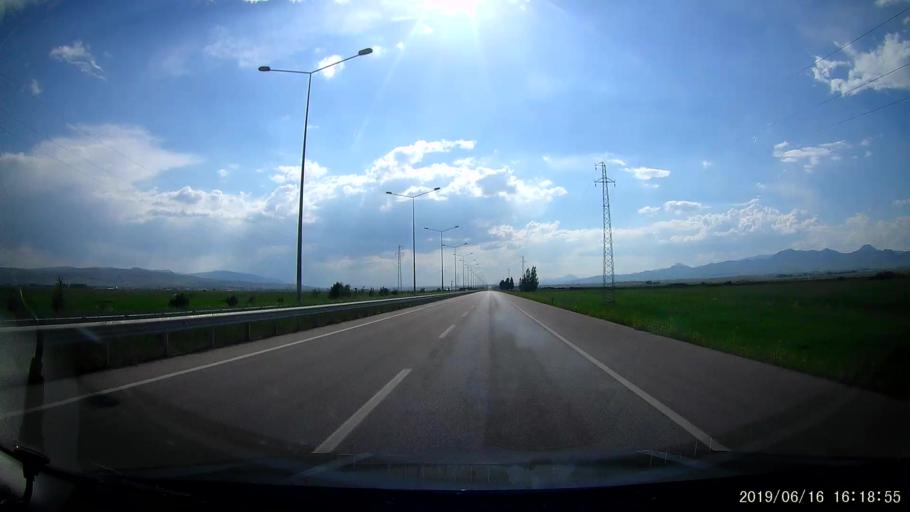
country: TR
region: Erzurum
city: Ilica
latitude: 39.9657
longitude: 41.1547
